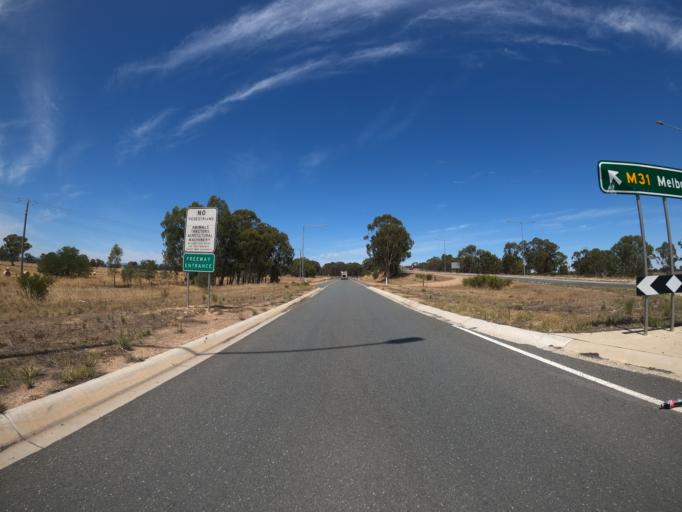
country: AU
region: Victoria
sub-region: Benalla
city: Benalla
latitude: -36.5202
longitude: 146.0650
